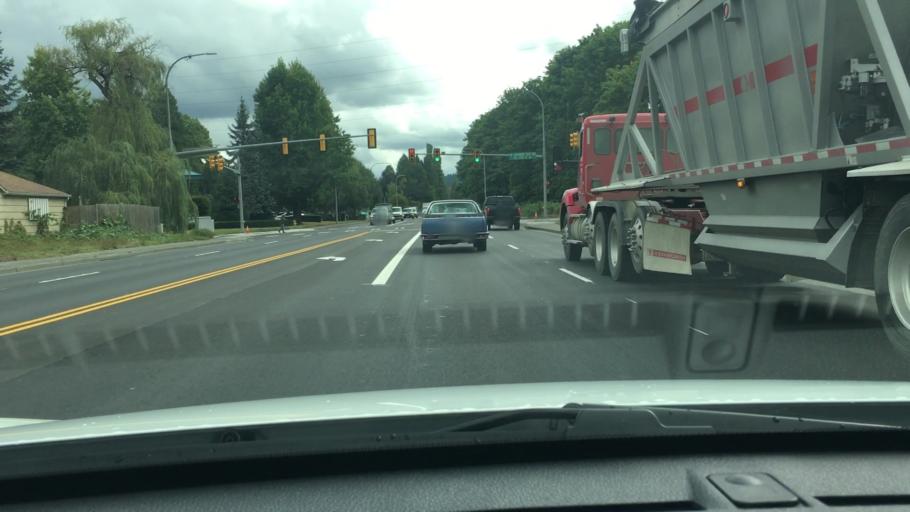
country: US
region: Washington
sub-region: King County
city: Fairwood
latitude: 47.4758
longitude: -122.1766
